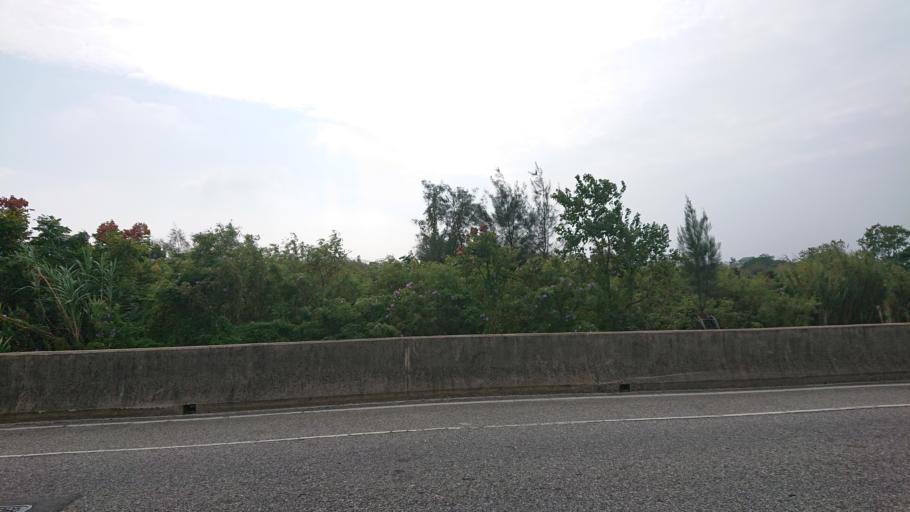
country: TW
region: Fukien
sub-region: Kinmen
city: Jincheng
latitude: 24.4493
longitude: 118.3835
